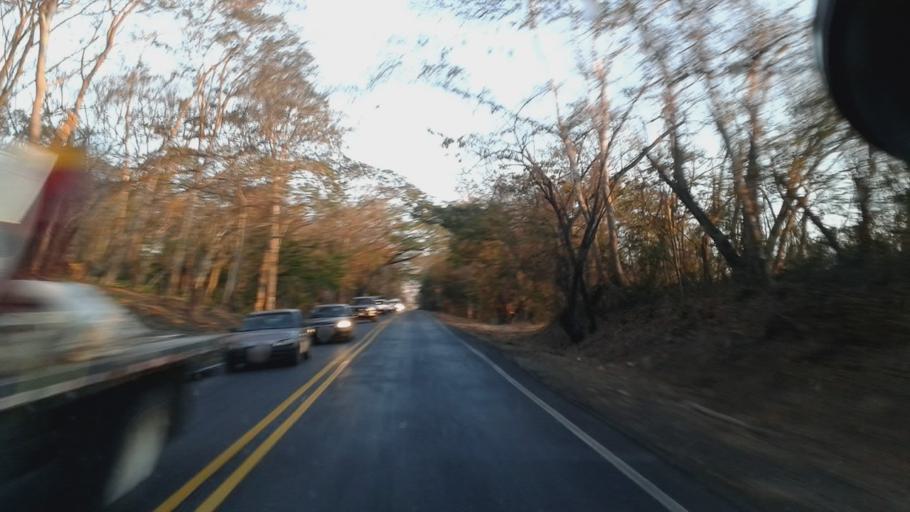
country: CR
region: Guanacaste
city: Juntas
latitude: 10.1285
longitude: -84.9015
